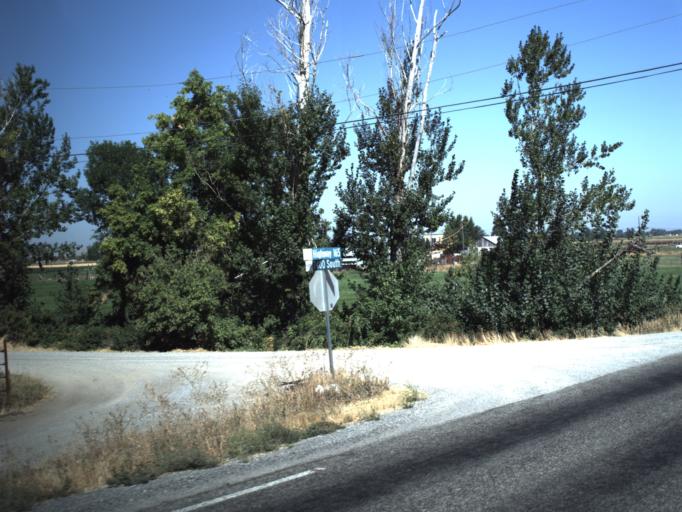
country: US
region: Utah
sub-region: Cache County
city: Hyrum
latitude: 41.5982
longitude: -111.8348
